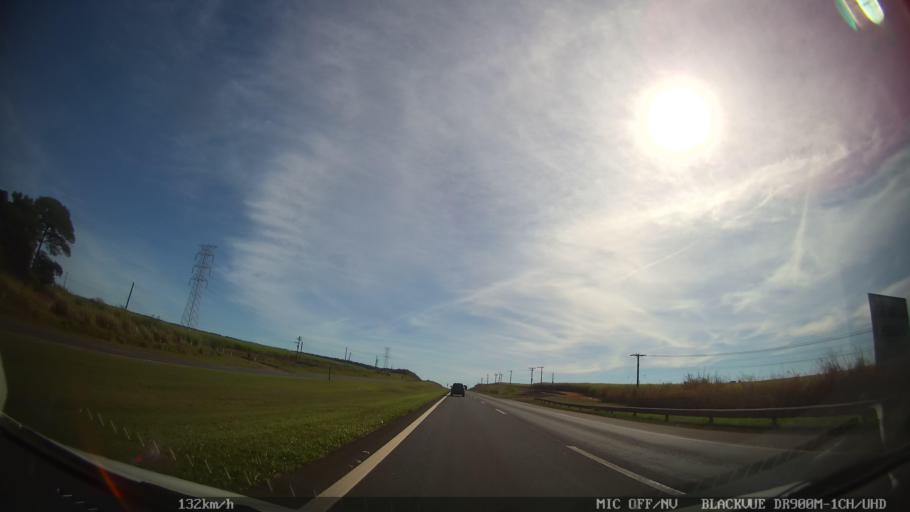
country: BR
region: Sao Paulo
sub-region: Araras
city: Araras
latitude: -22.3027
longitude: -47.3920
